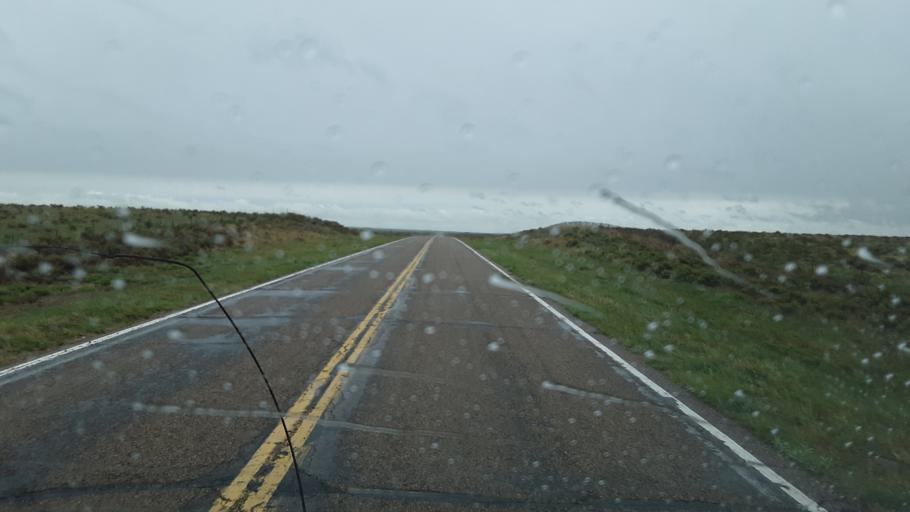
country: US
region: Colorado
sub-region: Lincoln County
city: Hugo
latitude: 38.8496
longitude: -103.1702
